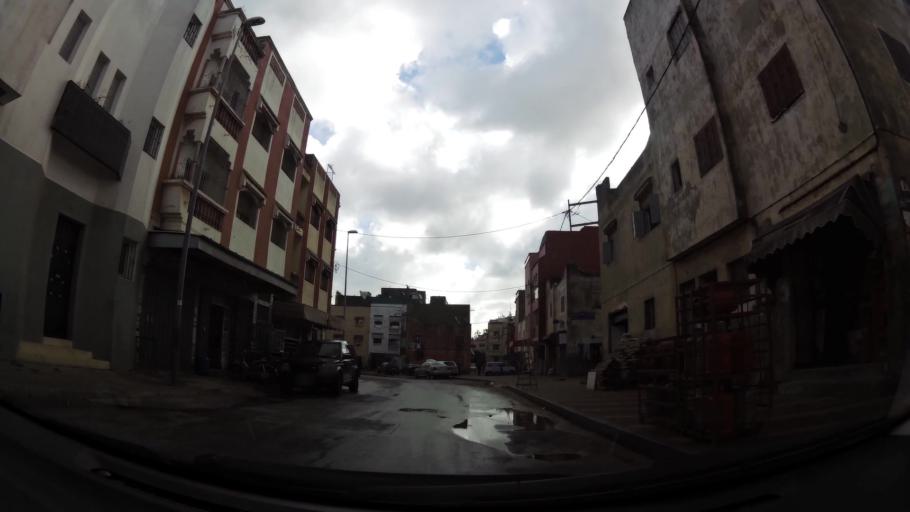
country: MA
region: Grand Casablanca
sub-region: Casablanca
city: Casablanca
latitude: 33.5604
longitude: -7.6804
